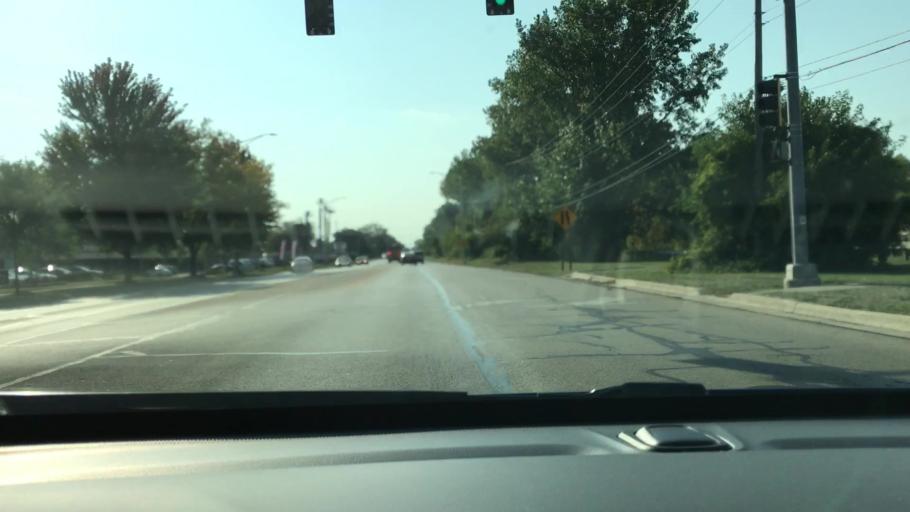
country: US
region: Illinois
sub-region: DuPage County
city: Warrenville
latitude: 41.7815
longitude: -88.2134
